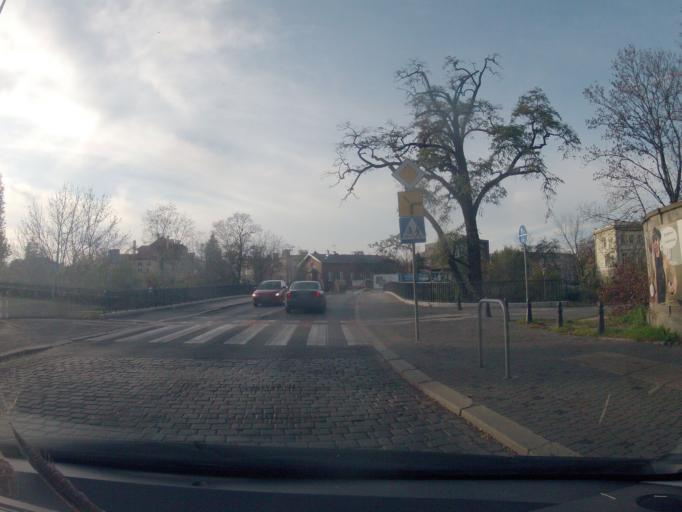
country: PL
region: Opole Voivodeship
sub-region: Powiat opolski
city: Opole
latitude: 50.6627
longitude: 17.9228
